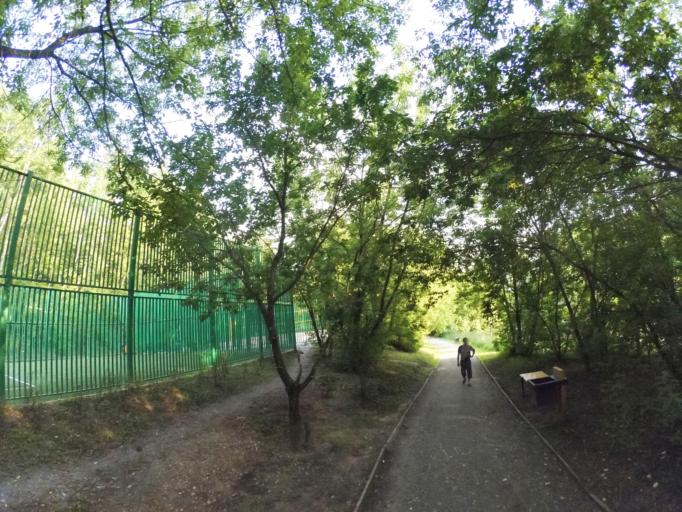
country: RU
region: Moscow
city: Shchukino
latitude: 55.8031
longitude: 37.4492
